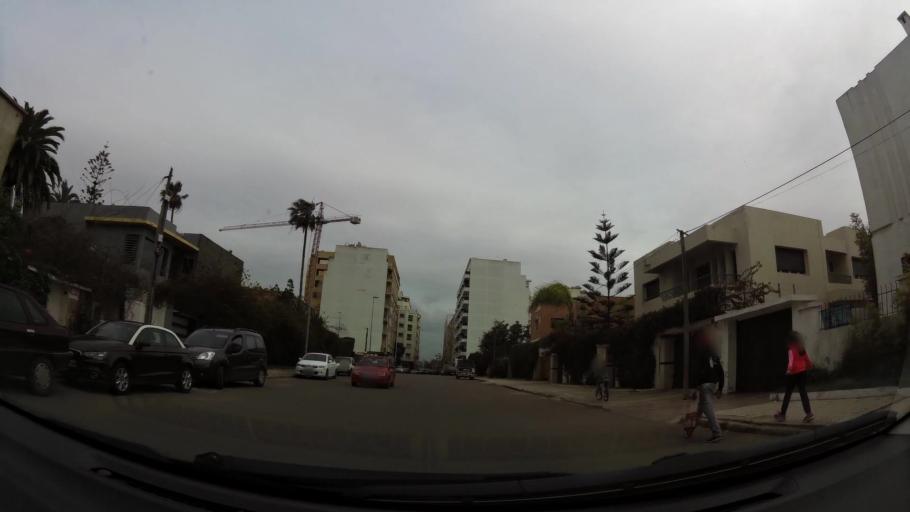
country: MA
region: Grand Casablanca
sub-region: Casablanca
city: Casablanca
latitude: 33.5967
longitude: -7.6530
